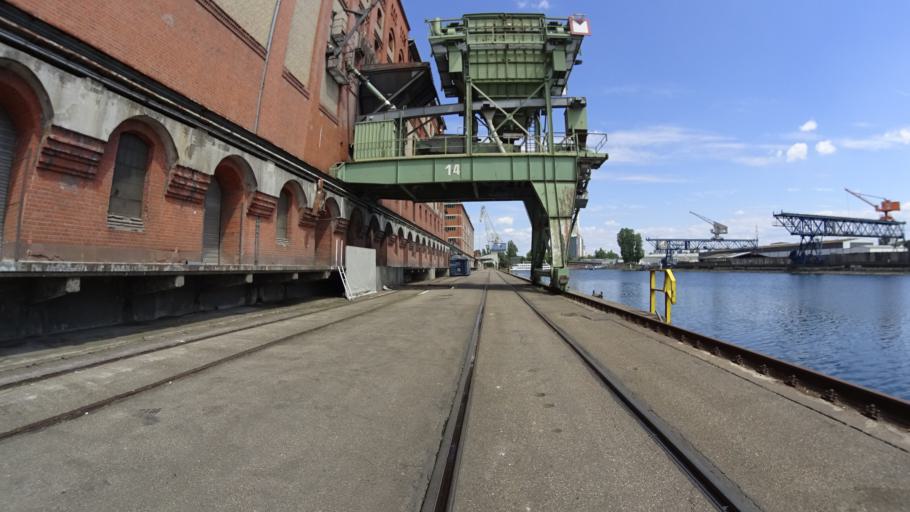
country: DE
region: Baden-Wuerttemberg
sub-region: Karlsruhe Region
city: Rheinstetten
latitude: 49.0156
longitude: 8.3385
